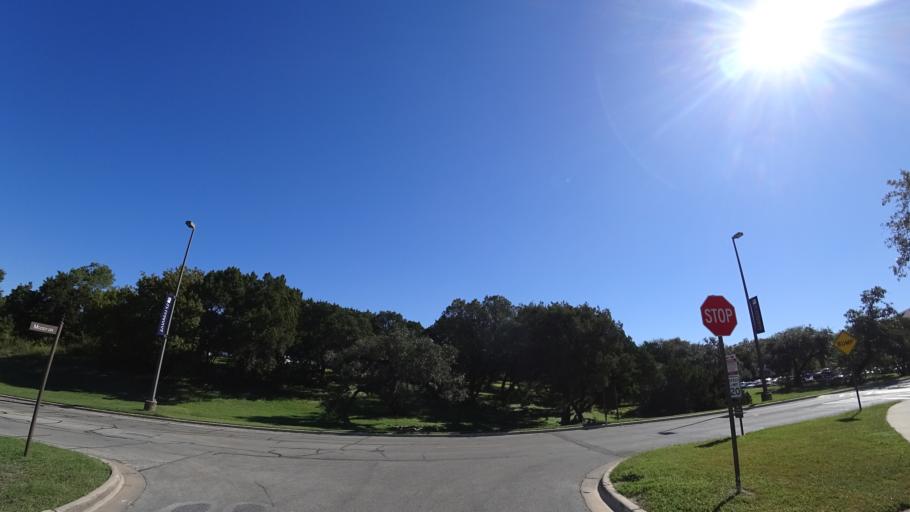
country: US
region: Texas
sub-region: Travis County
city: Austin
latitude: 30.2323
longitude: -97.7576
